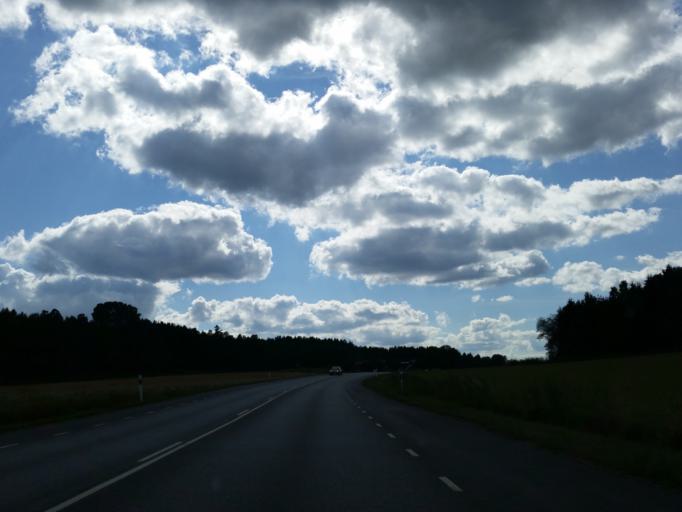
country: SE
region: Soedermanland
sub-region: Trosa Kommun
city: Vagnharad
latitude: 58.9486
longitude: 17.5415
